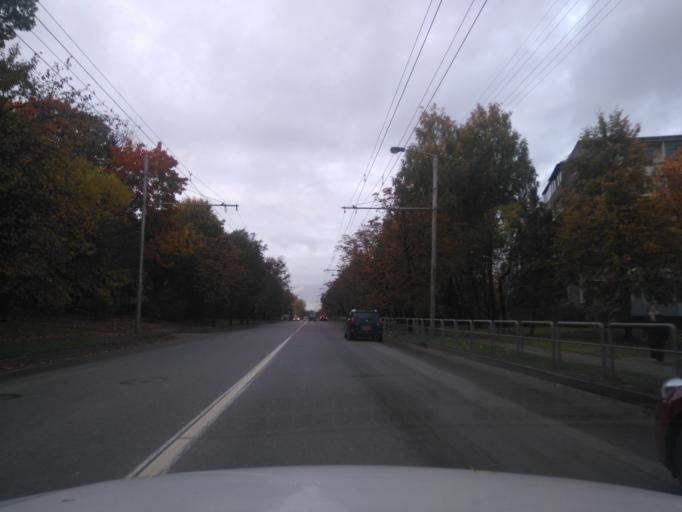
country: LT
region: Kauno apskritis
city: Dainava (Kaunas)
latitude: 54.9074
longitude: 23.9738
